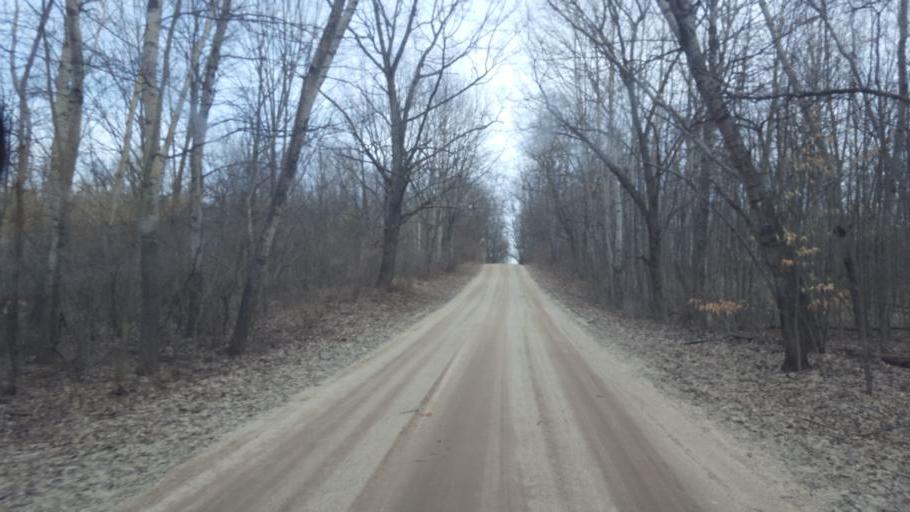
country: US
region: Michigan
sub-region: Isabella County
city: Lake Isabella
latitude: 43.6792
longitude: -85.1347
